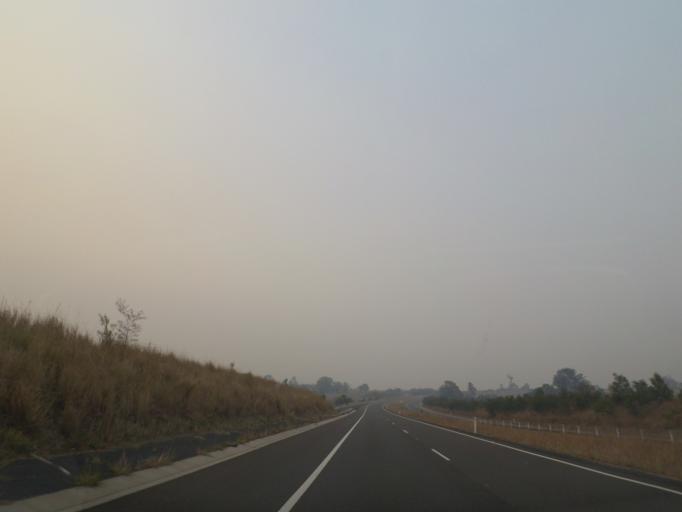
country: AU
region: New South Wales
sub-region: Nambucca Shire
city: Macksville
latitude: -30.7633
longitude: 152.9040
